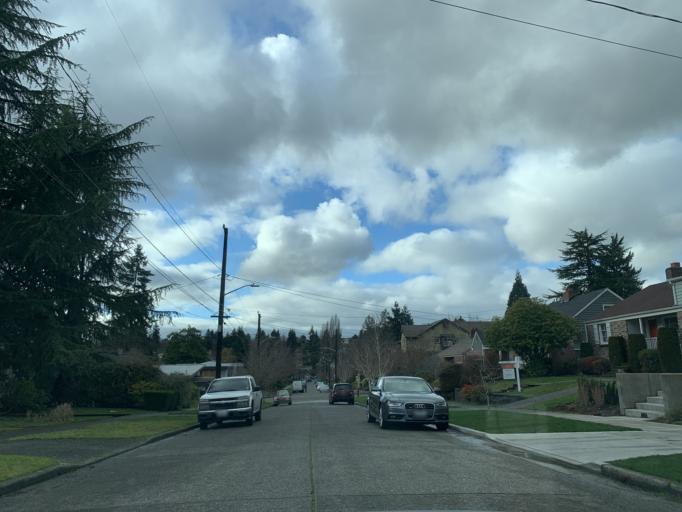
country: US
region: Washington
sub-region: King County
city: Yarrow Point
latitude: 47.6695
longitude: -122.2811
